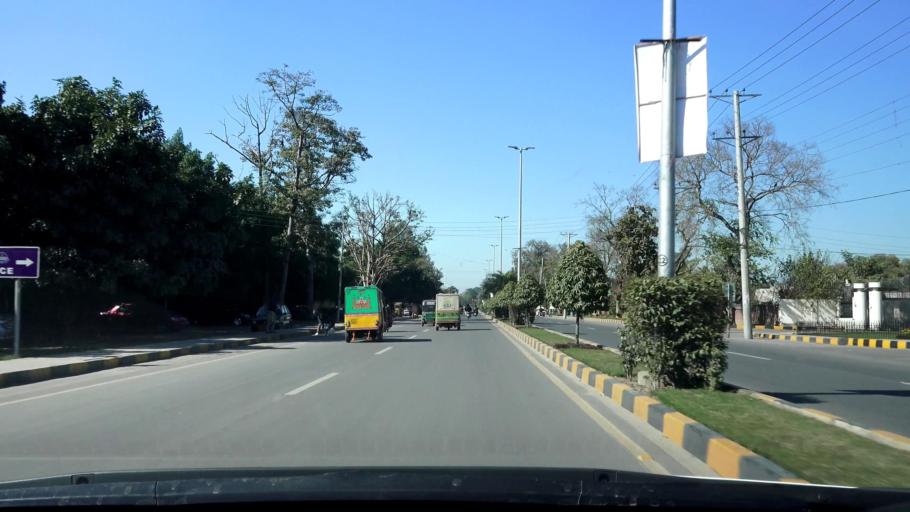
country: PK
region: Punjab
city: Faisalabad
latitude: 31.4239
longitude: 73.0817
